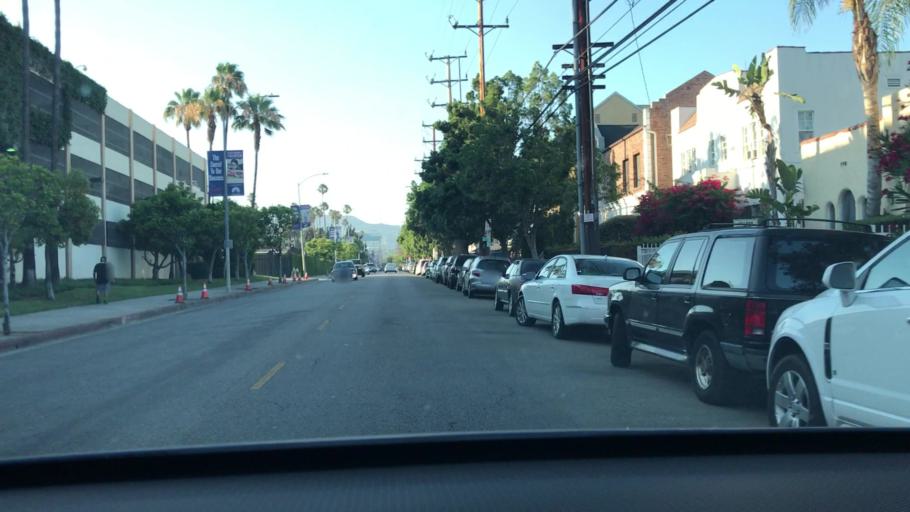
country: US
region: California
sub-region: Los Angeles County
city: Hollywood
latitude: 34.0846
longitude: -118.3157
